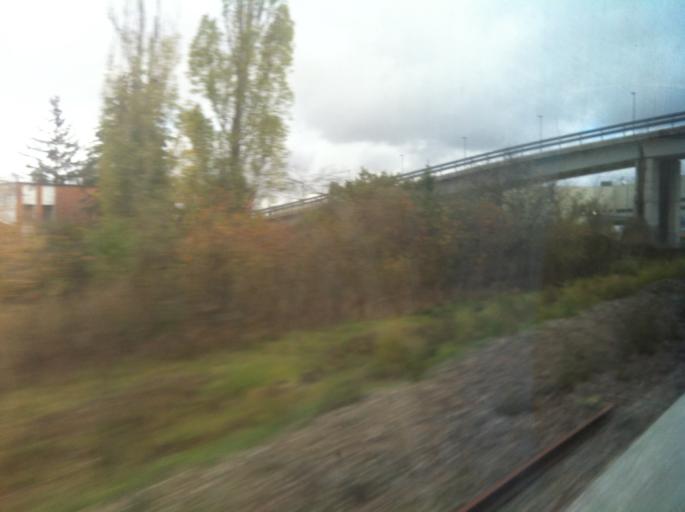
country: ES
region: Basque Country
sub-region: Provincia de Alava
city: Gasteiz / Vitoria
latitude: 42.8542
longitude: -2.7210
